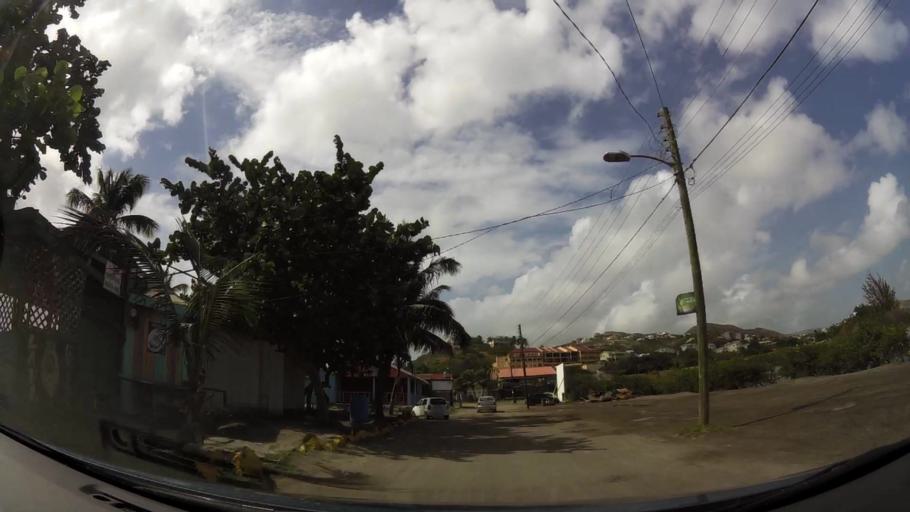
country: KN
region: Saint George Basseterre
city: Basseterre
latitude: 17.2816
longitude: -62.6889
